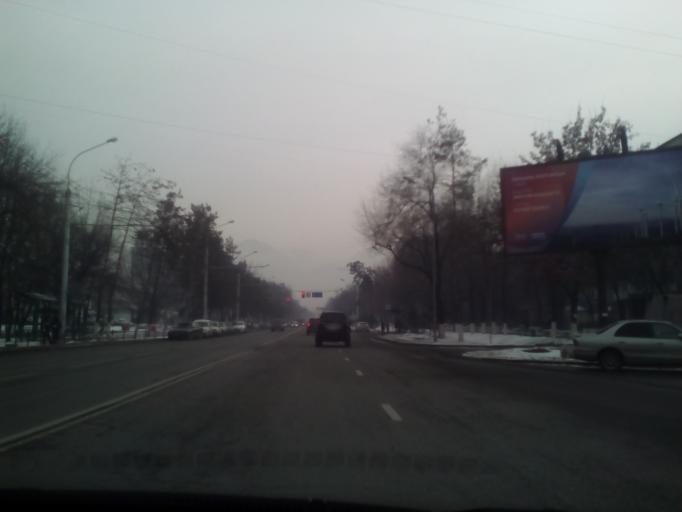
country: KZ
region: Almaty Qalasy
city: Almaty
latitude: 43.2363
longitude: 76.8306
